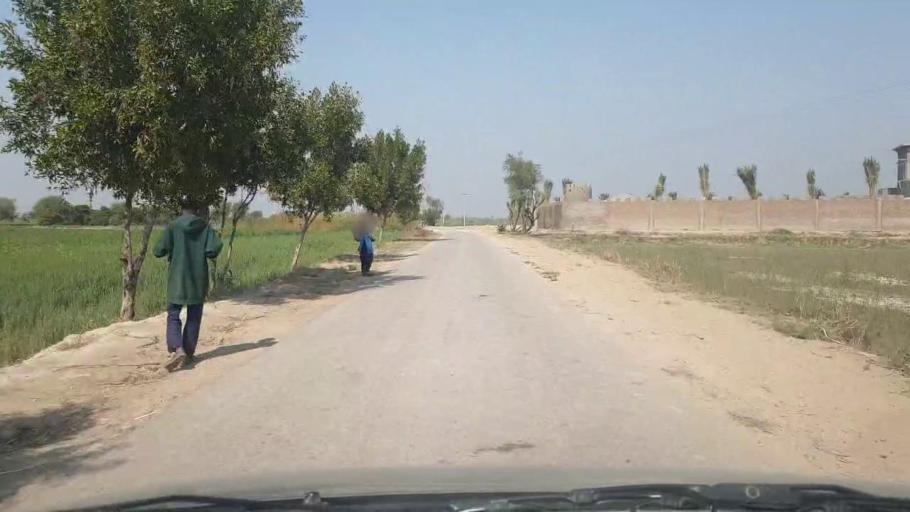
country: PK
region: Sindh
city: Mirwah Gorchani
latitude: 25.3189
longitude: 69.1530
